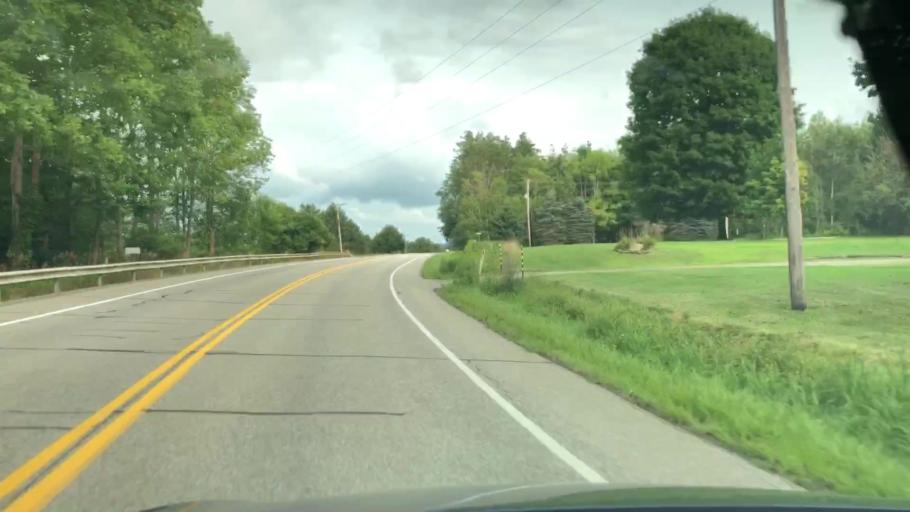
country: US
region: Pennsylvania
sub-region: Erie County
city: Northwest Harborcreek
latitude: 42.0606
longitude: -79.8704
